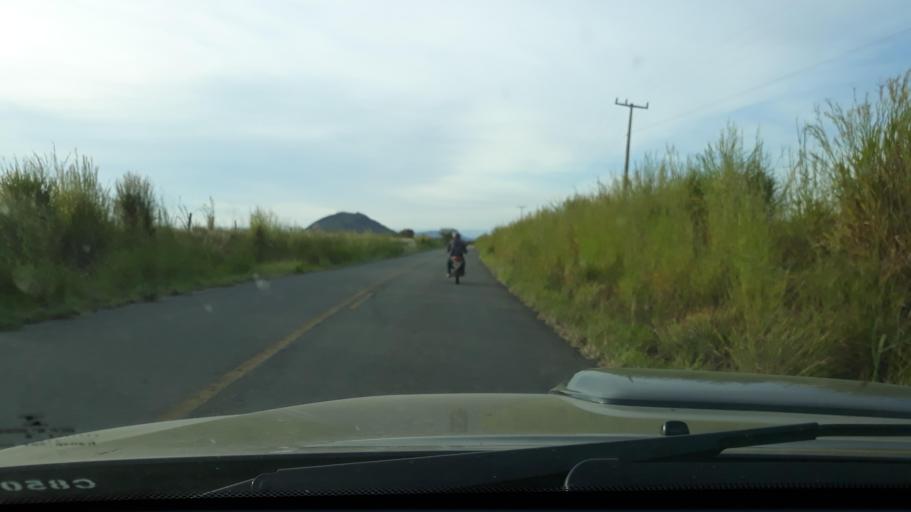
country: BR
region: Bahia
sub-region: Guanambi
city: Guanambi
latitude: -14.1535
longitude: -42.8205
